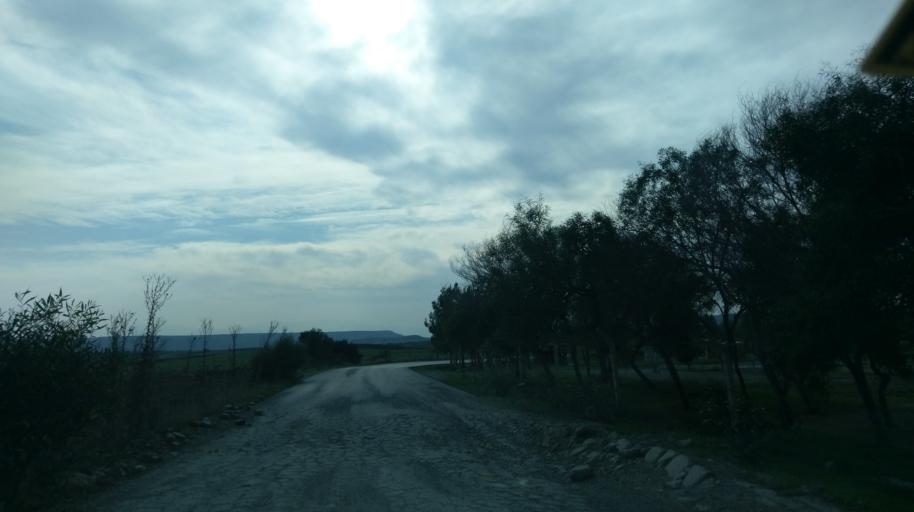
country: CY
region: Keryneia
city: Lapithos
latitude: 35.2874
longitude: 33.1268
